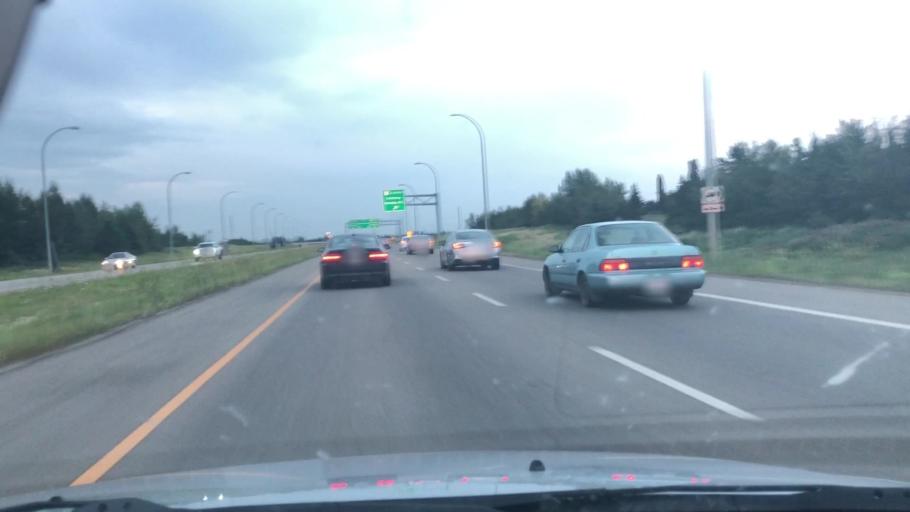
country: CA
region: Alberta
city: St. Albert
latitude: 53.5121
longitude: -113.6726
